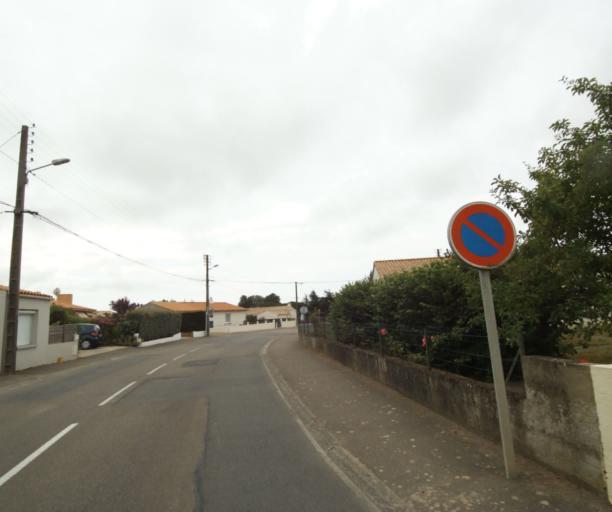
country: FR
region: Pays de la Loire
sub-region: Departement de la Vendee
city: Chateau-d'Olonne
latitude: 46.5015
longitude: -1.7332
